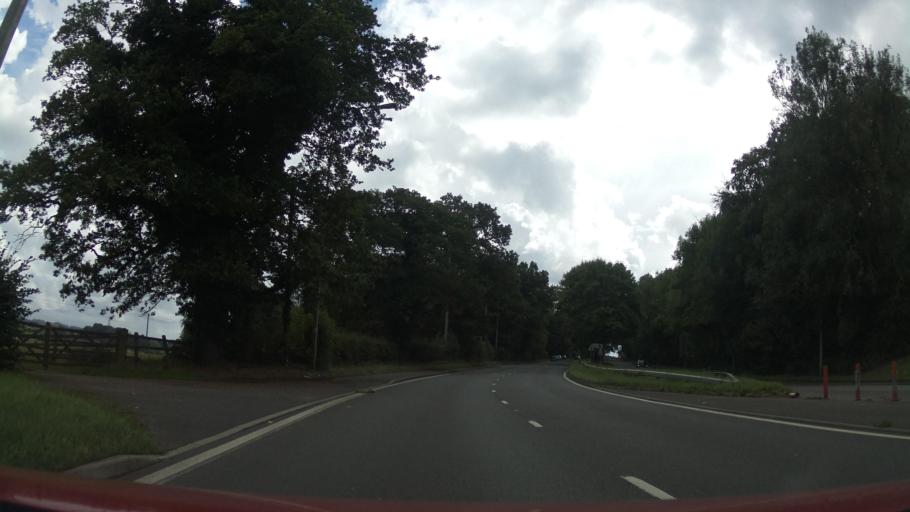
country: GB
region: England
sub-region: Staffordshire
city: Barlaston
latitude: 52.9473
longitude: -2.1903
